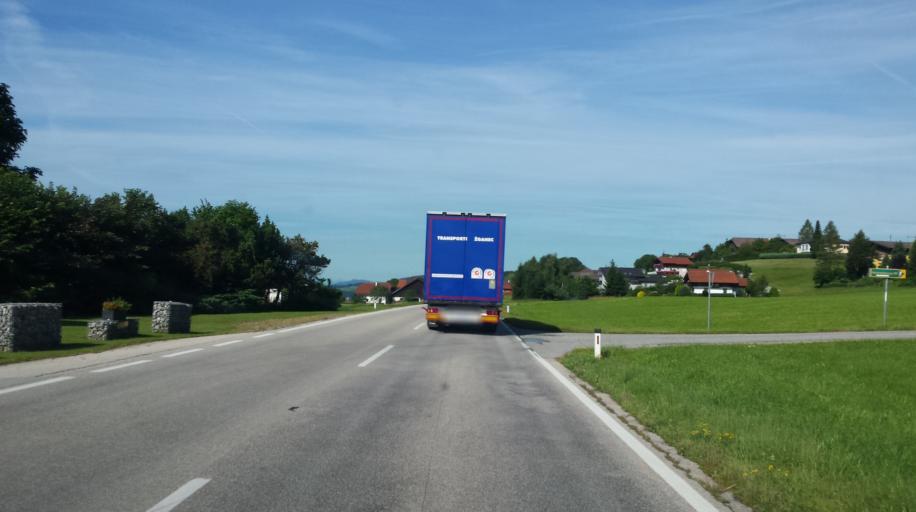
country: AT
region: Upper Austria
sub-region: Politischer Bezirk Vocklabruck
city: Oberhofen am Irrsee
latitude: 47.9922
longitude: 13.3037
